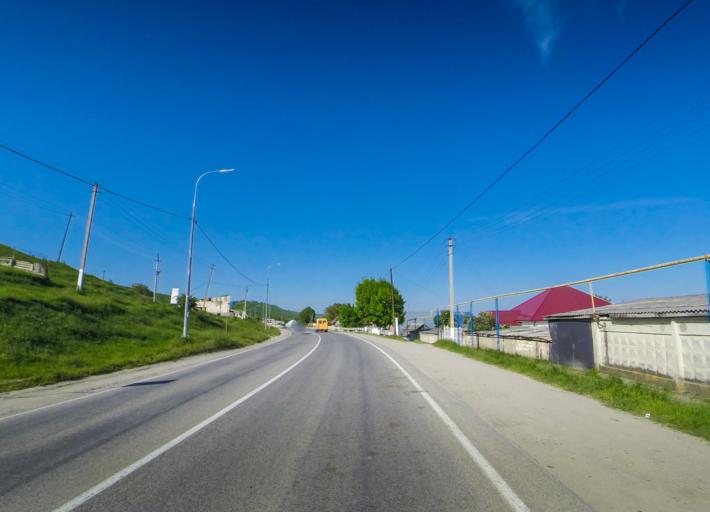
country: RU
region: Kabardino-Balkariya
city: Aushiger
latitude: 43.3975
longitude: 43.7404
